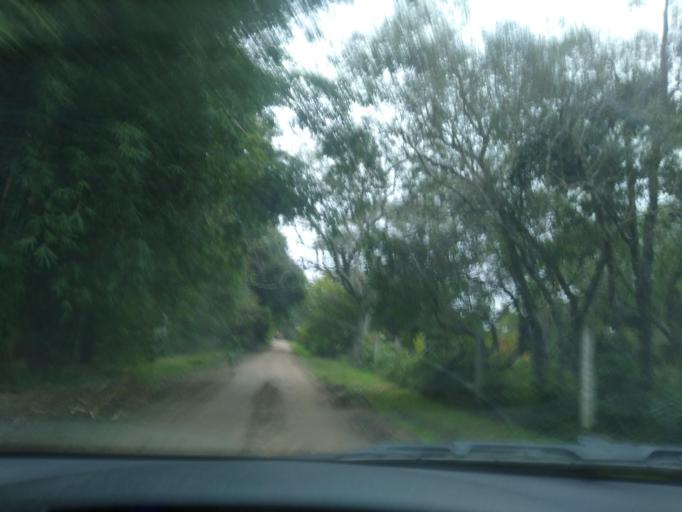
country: AR
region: Chaco
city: Colonia Benitez
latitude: -27.3310
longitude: -58.9533
